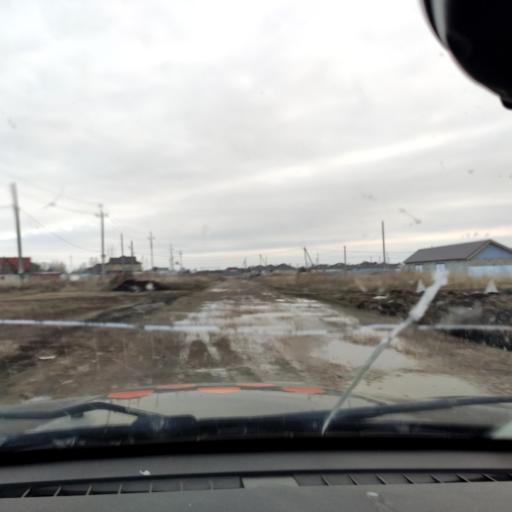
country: RU
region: Samara
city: Podstepki
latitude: 53.5243
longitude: 49.1684
